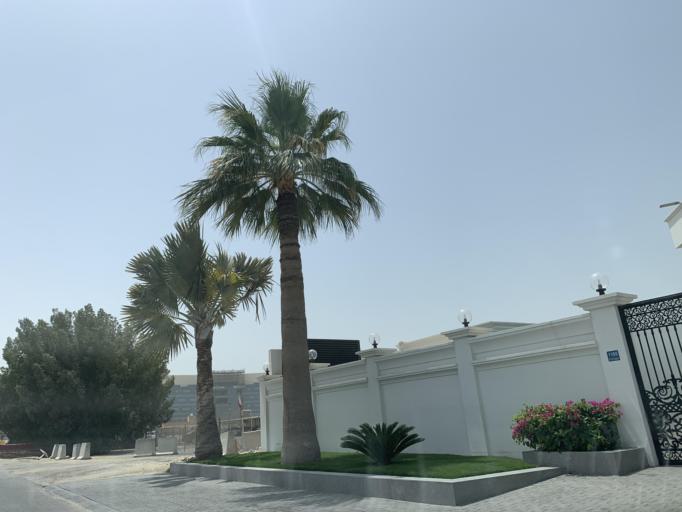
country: BH
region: Northern
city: Madinat `Isa
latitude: 26.1606
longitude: 50.5276
